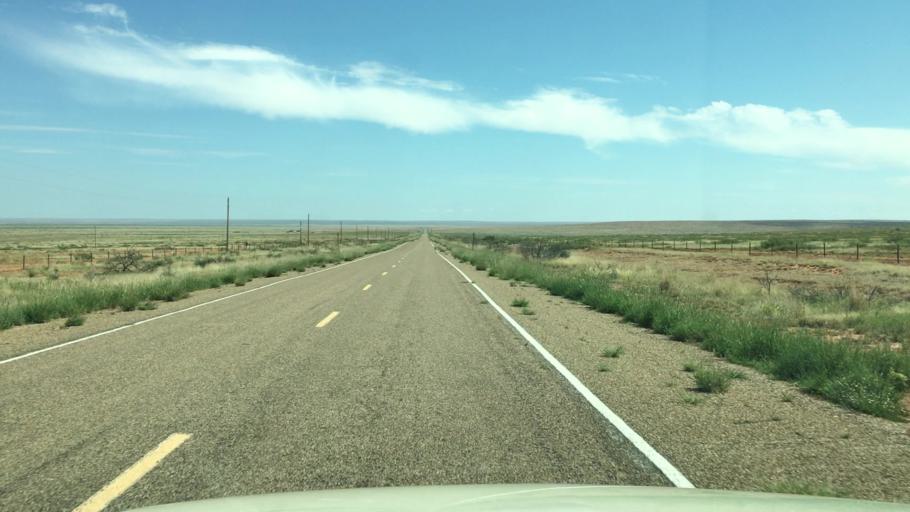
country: US
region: New Mexico
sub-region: De Baca County
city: Fort Sumner
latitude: 33.9853
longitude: -104.5728
